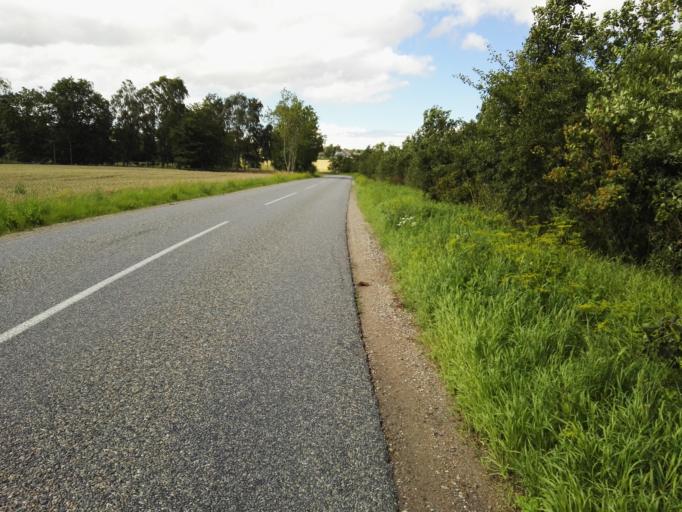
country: DK
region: Capital Region
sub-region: Egedal Kommune
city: Ganlose
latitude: 55.7925
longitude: 12.2297
